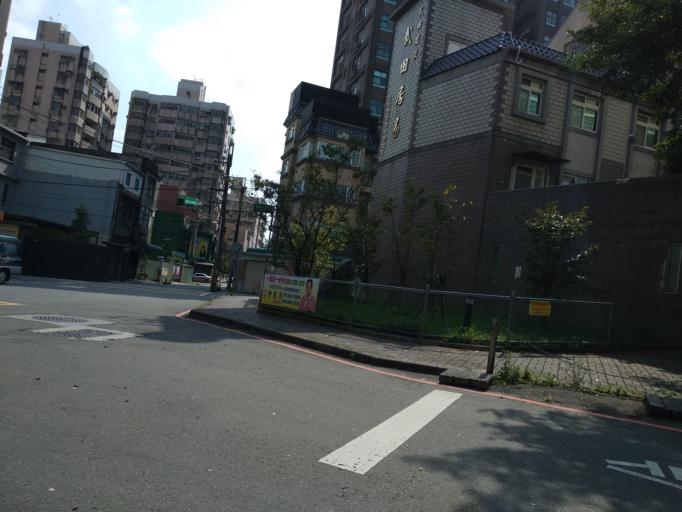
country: TW
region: Taiwan
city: Taoyuan City
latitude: 24.9448
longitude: 121.2059
